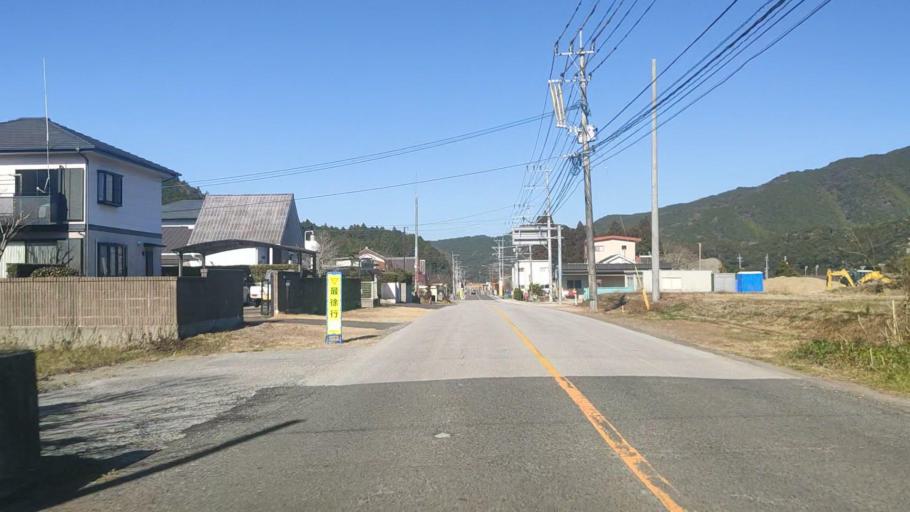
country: JP
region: Oita
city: Saiki
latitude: 32.9186
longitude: 131.9279
